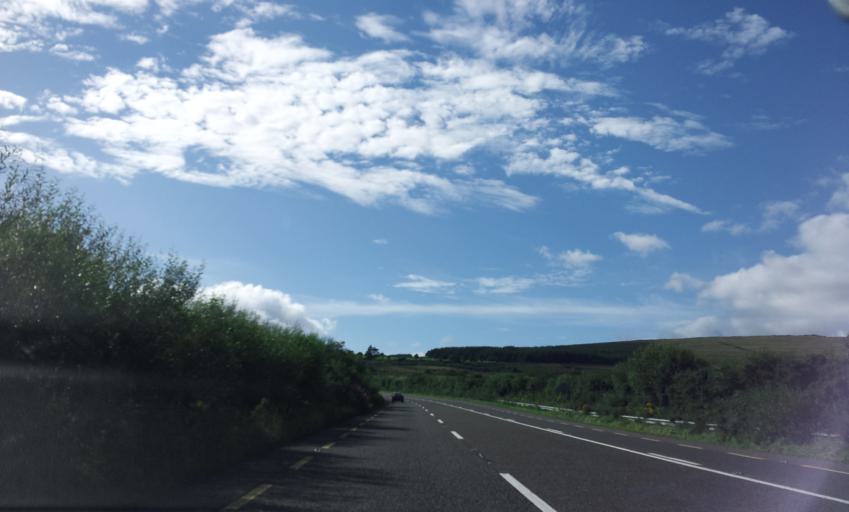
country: IE
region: Munster
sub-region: County Cork
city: Millstreet
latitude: 51.9617
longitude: -9.2050
